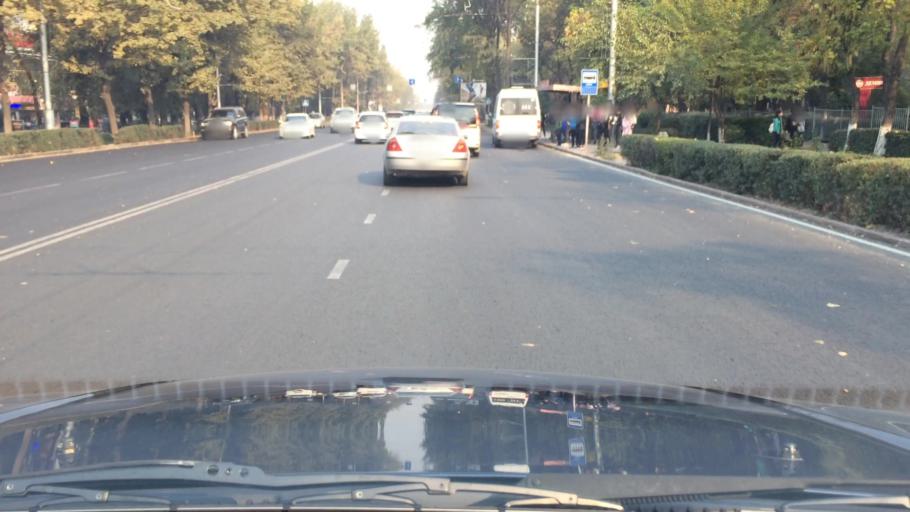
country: KG
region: Chuy
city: Bishkek
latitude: 42.8486
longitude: 74.5864
